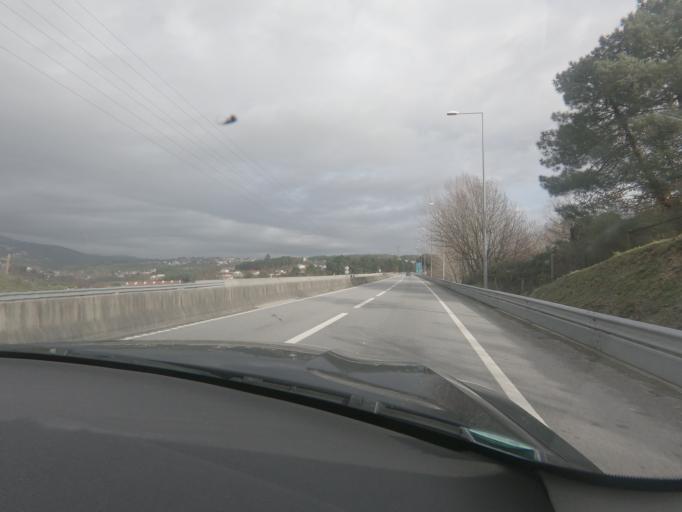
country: PT
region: Vila Real
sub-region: Vila Real
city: Vila Real
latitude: 41.3133
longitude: -7.7412
